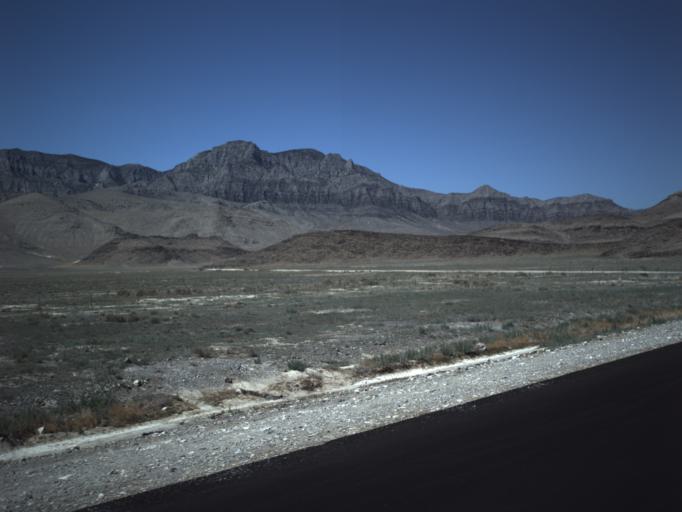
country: US
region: Utah
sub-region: Beaver County
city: Milford
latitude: 39.0526
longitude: -113.4233
